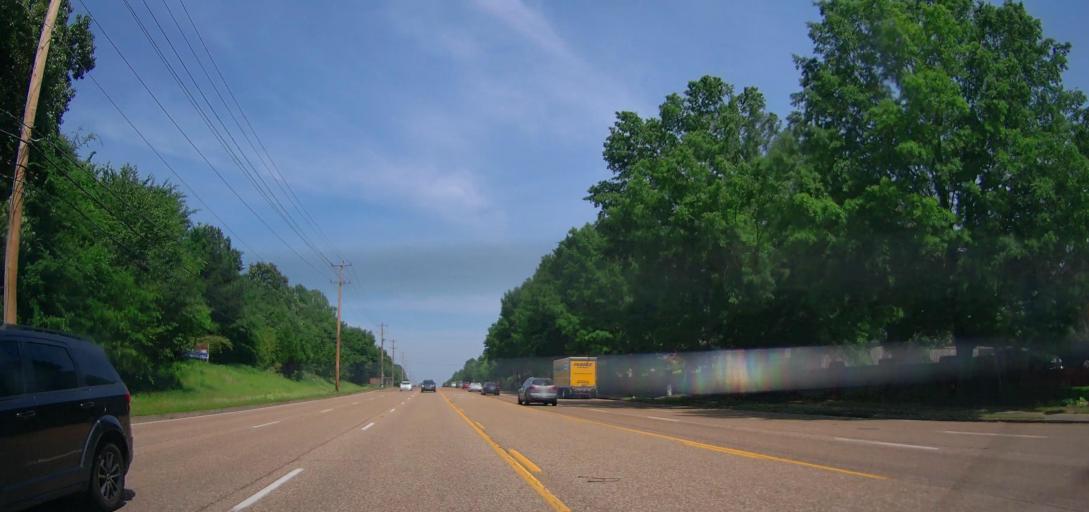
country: US
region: Mississippi
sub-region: De Soto County
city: Olive Branch
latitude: 35.0205
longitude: -89.8171
